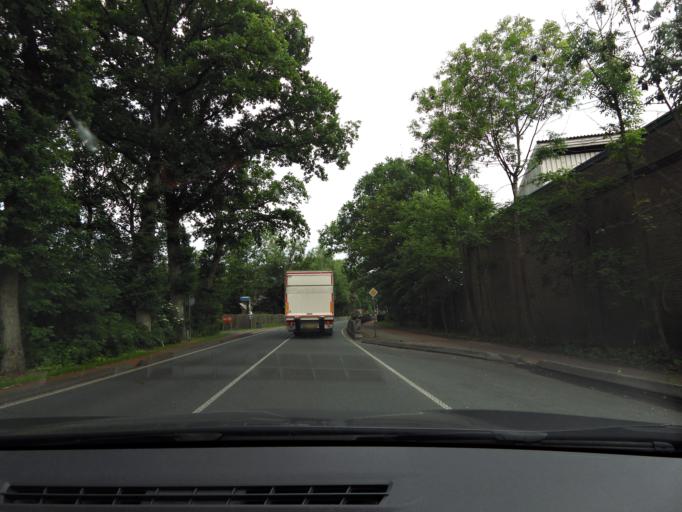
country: NL
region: Gelderland
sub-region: Gemeente Brummen
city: Eerbeek
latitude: 52.0961
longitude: 6.0542
